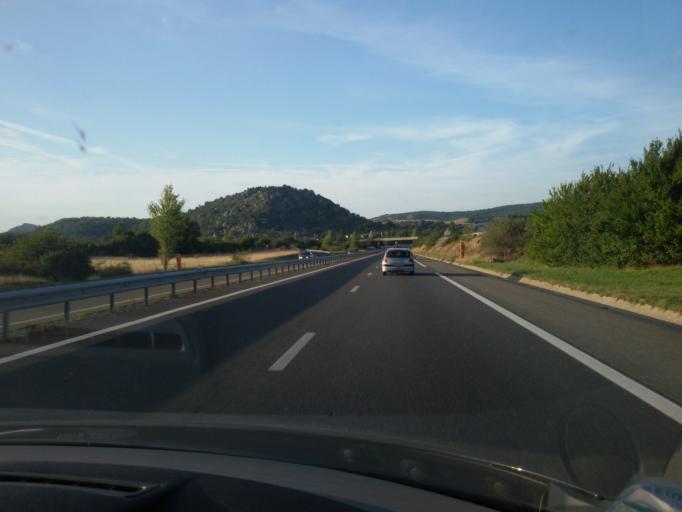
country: FR
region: Languedoc-Roussillon
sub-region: Departement de l'Herault
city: Lodeve
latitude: 43.8626
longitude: 3.3103
